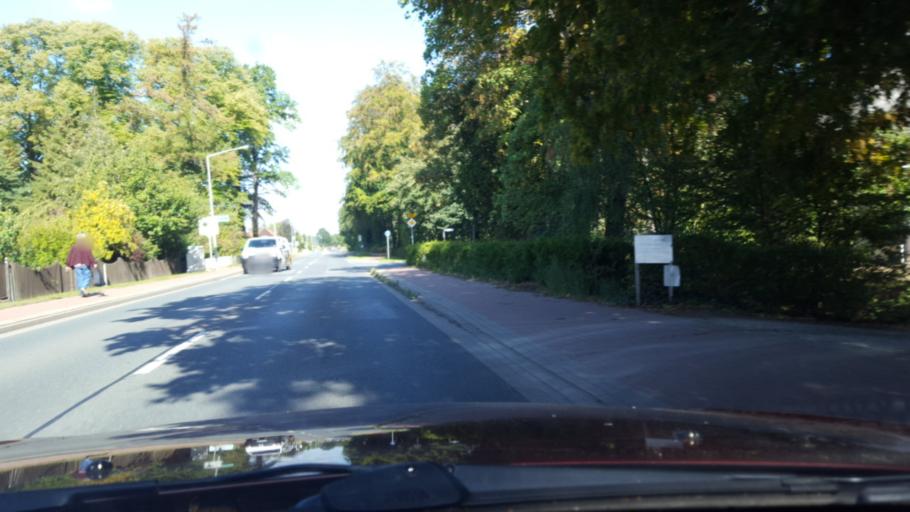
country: DE
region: Lower Saxony
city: Eystrup
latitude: 52.7809
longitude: 9.2125
